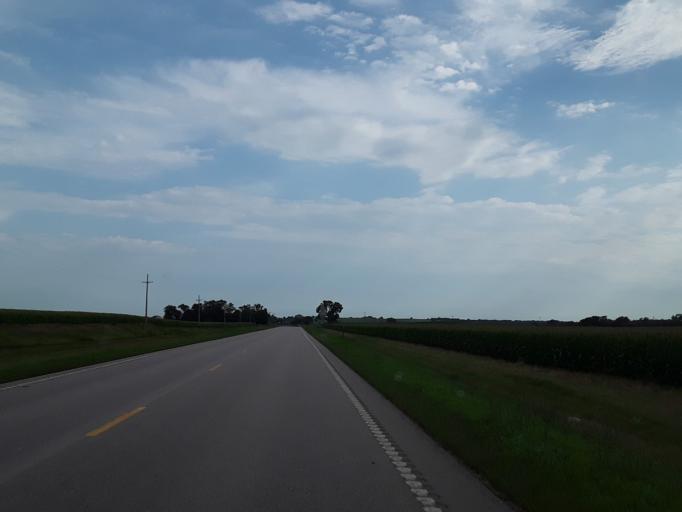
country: US
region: Nebraska
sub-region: Saunders County
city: Ashland
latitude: 41.1014
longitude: -96.4259
